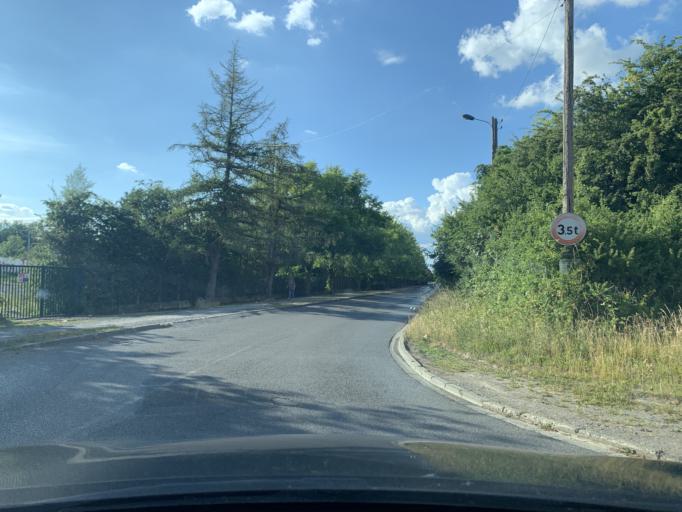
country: FR
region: Nord-Pas-de-Calais
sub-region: Departement du Nord
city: Cambrai
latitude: 50.1734
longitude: 3.2578
